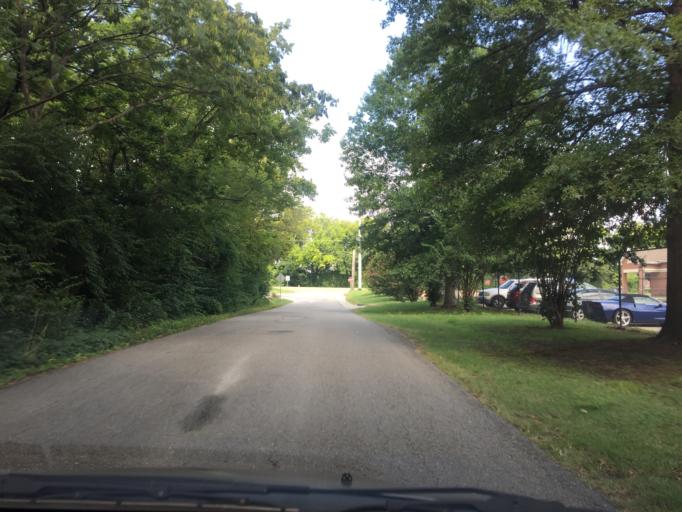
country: US
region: Tennessee
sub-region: Hamilton County
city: East Chattanooga
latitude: 35.0696
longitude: -85.2692
